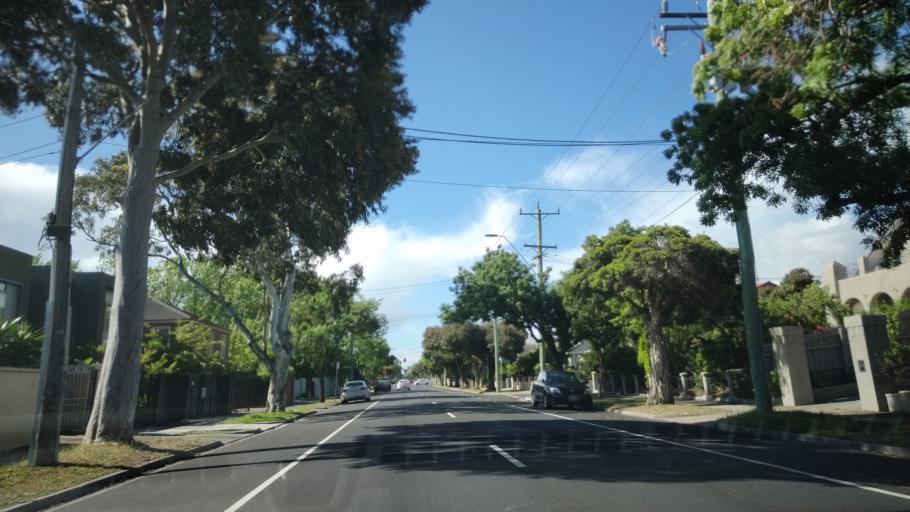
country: AU
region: Victoria
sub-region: Glen Eira
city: Caulfield
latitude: -37.8826
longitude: 145.0297
